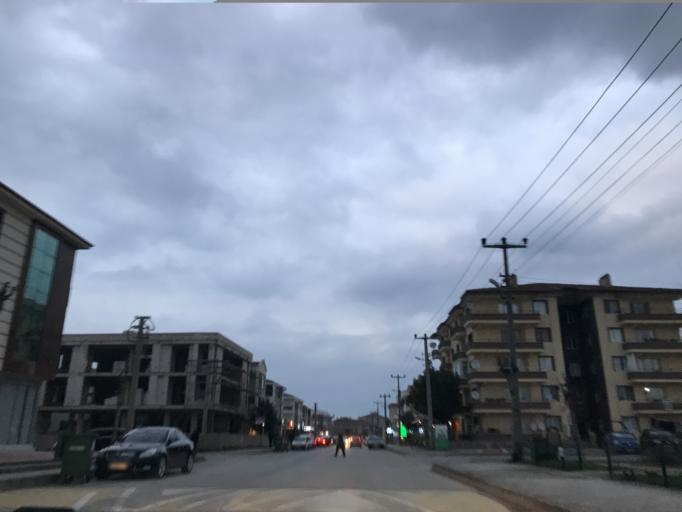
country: TR
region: Yalova
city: Yalova
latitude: 40.6447
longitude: 29.2598
